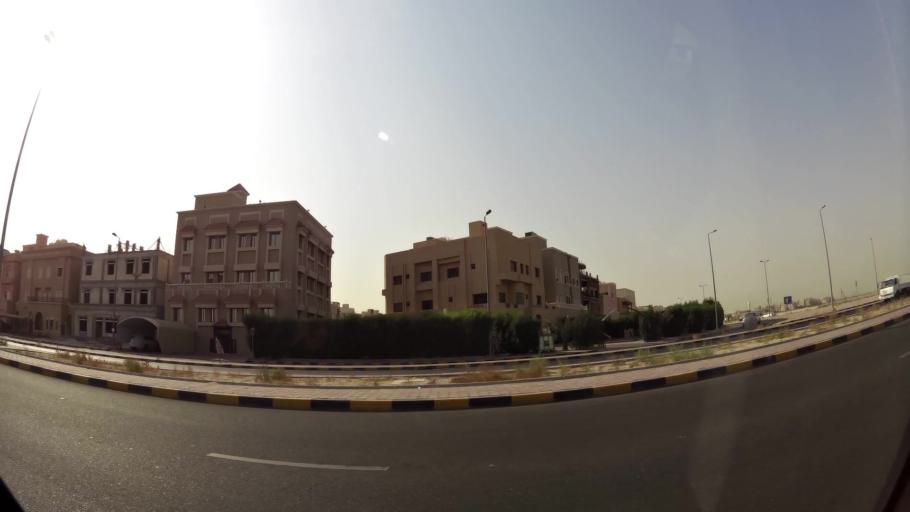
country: KW
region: Muhafazat al Jahra'
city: Al Jahra'
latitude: 29.3403
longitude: 47.7858
